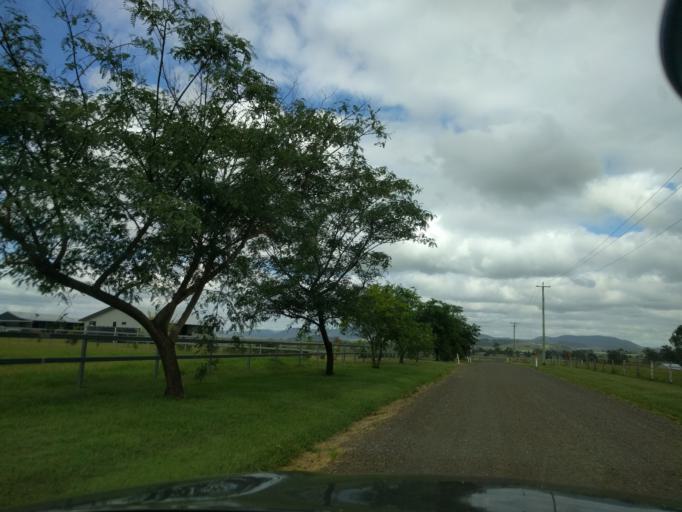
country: AU
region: Queensland
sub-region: Logan
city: Cedar Vale
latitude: -28.0083
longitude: 152.9948
